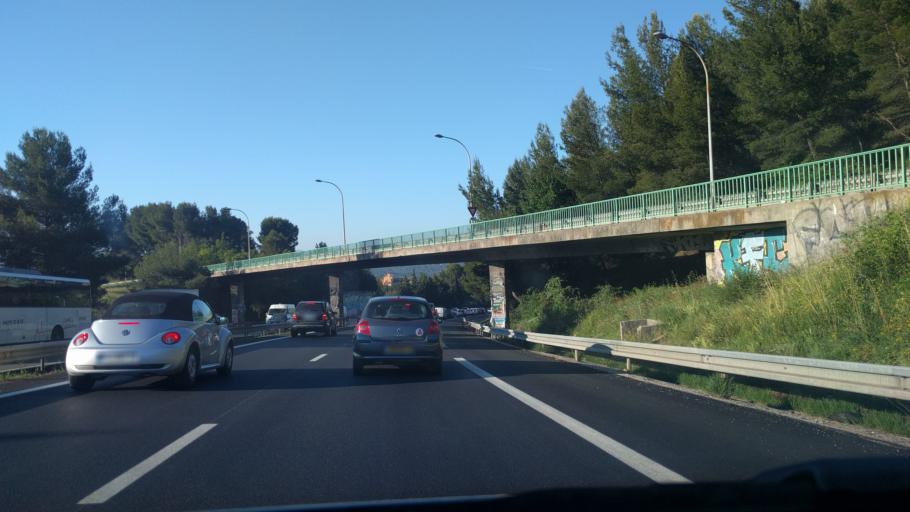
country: FR
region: Provence-Alpes-Cote d'Azur
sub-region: Departement des Bouches-du-Rhone
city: Aix-en-Provence
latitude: 43.5402
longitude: 5.4326
